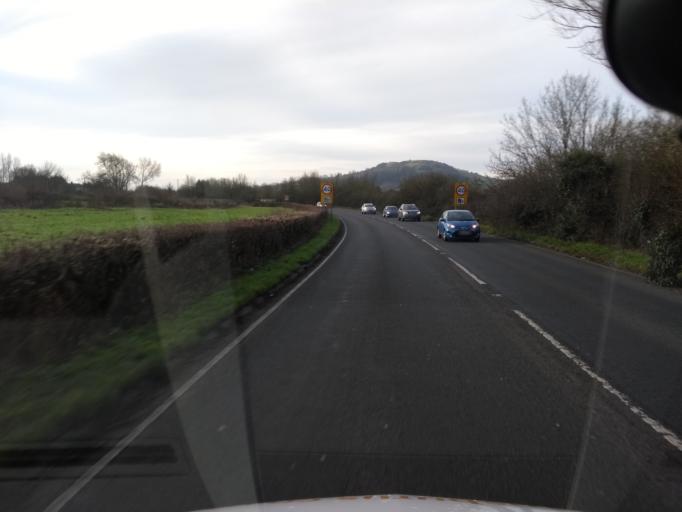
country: GB
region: England
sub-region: North Somerset
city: Bleadon
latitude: 51.2668
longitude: -2.9350
